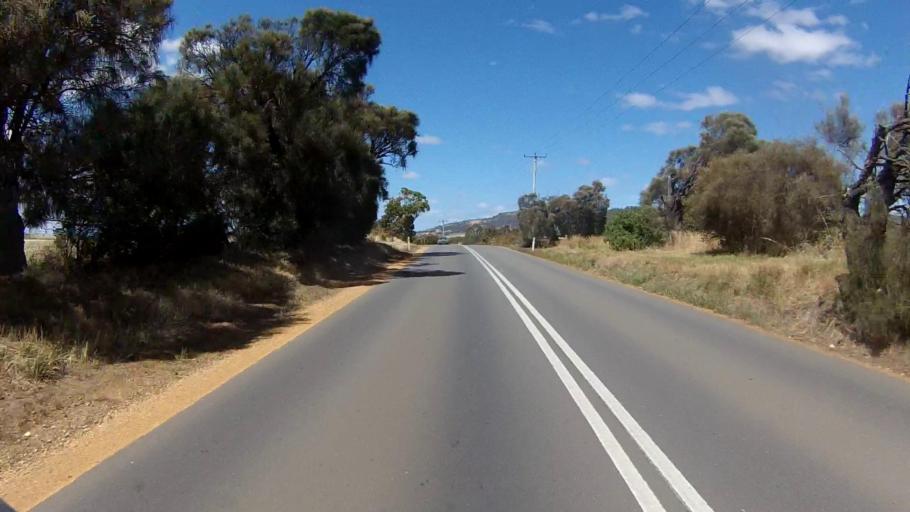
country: AU
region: Tasmania
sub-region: Clarence
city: Cambridge
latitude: -42.7632
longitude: 147.4148
